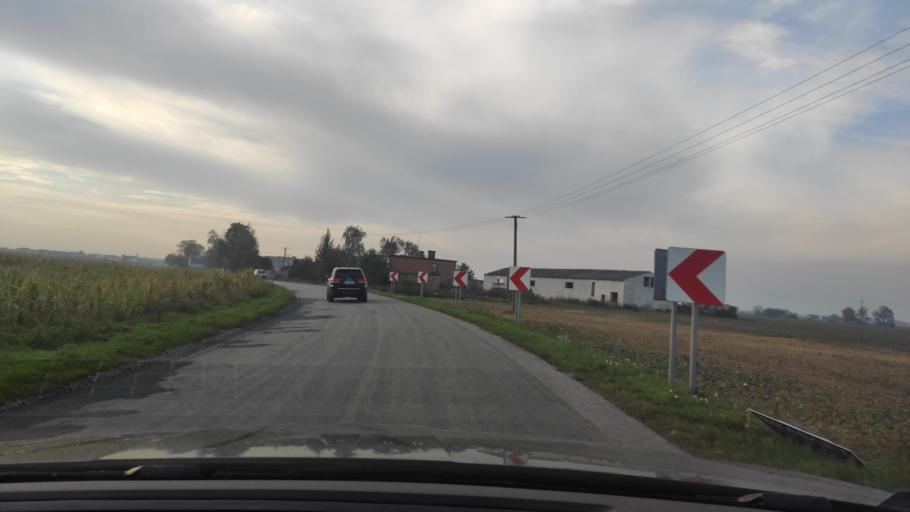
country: PL
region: Greater Poland Voivodeship
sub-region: Powiat poznanski
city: Kleszczewo
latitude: 52.3671
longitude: 17.1676
